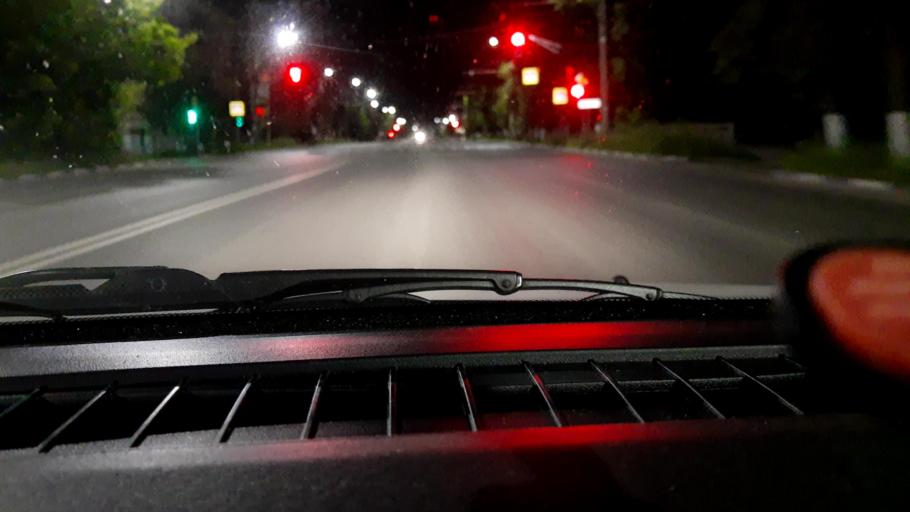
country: RU
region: Nizjnij Novgorod
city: Dzerzhinsk
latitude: 56.2416
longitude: 43.4815
